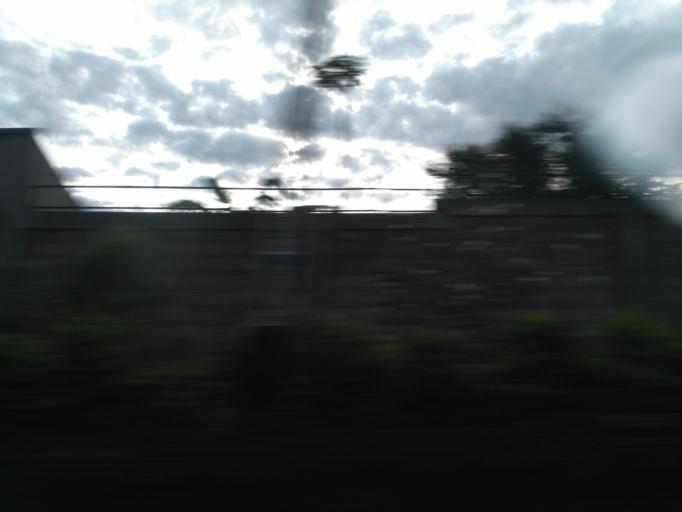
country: UG
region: Eastern Region
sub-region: Jinja District
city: Jinja
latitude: 0.4436
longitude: 33.2029
